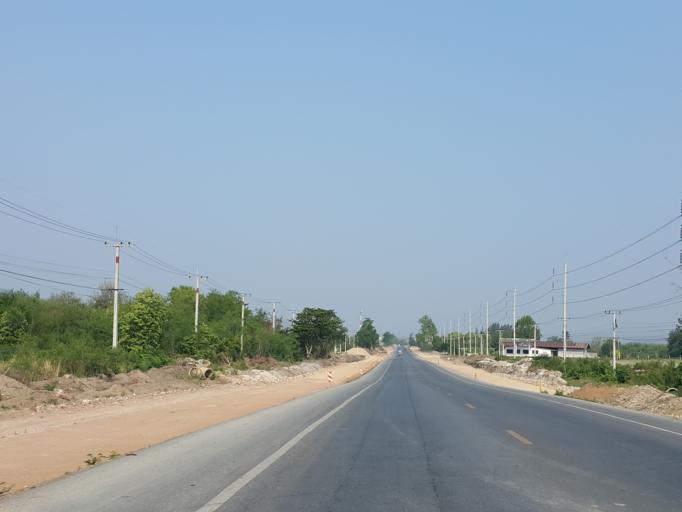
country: TH
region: Kanchanaburi
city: Sai Yok
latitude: 14.0875
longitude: 99.3365
